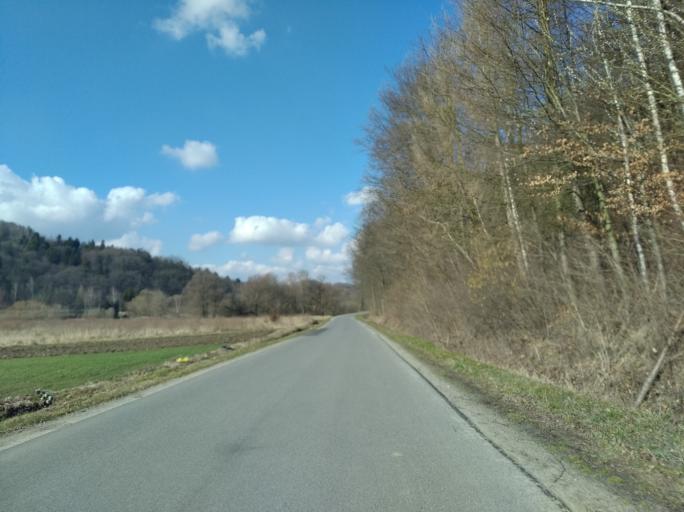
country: PL
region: Subcarpathian Voivodeship
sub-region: Powiat strzyzowski
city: Frysztak
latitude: 49.8504
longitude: 21.6245
